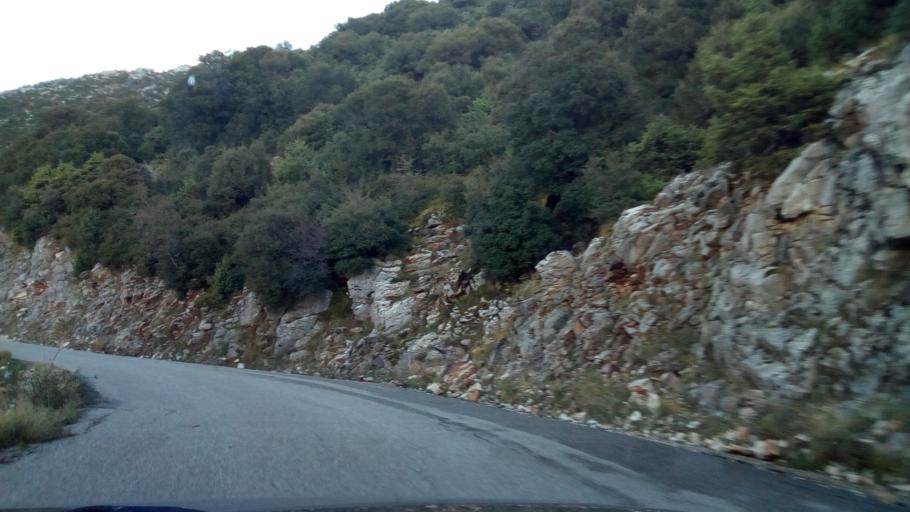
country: GR
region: West Greece
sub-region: Nomos Aitolias kai Akarnanias
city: Nafpaktos
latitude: 38.5177
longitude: 21.8488
